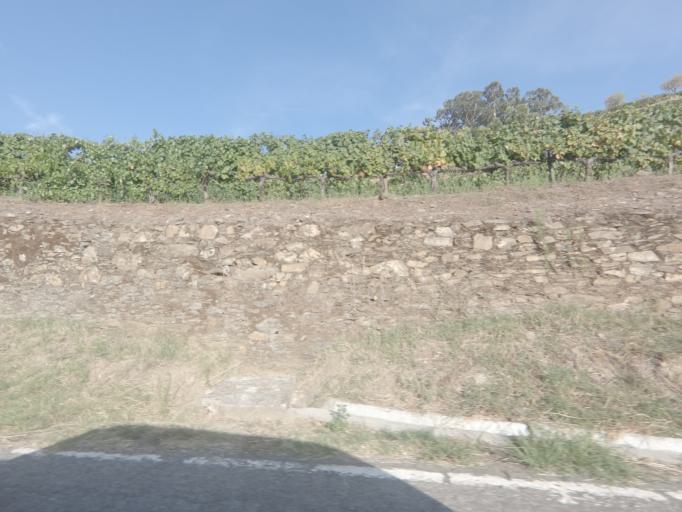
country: PT
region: Vila Real
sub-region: Sabrosa
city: Sabrosa
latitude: 41.2143
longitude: -7.5406
